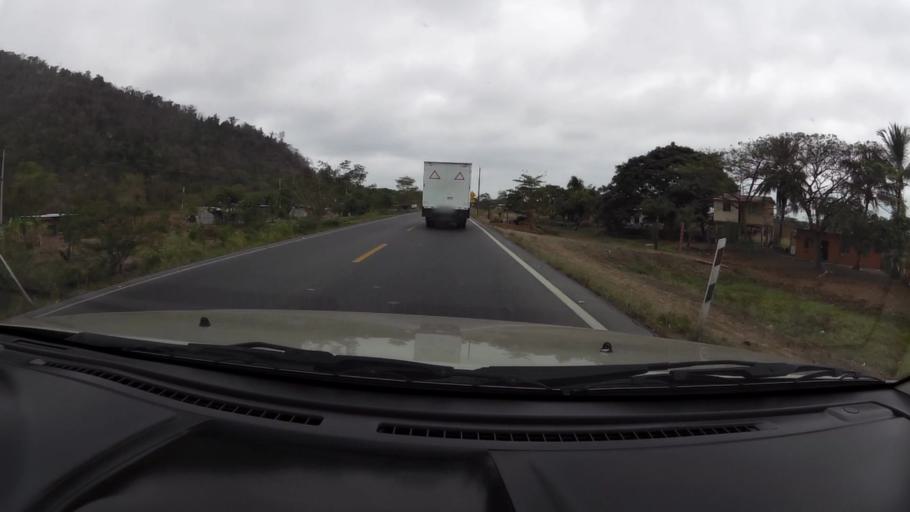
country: EC
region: Guayas
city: Naranjal
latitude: -2.4492
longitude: -79.6277
